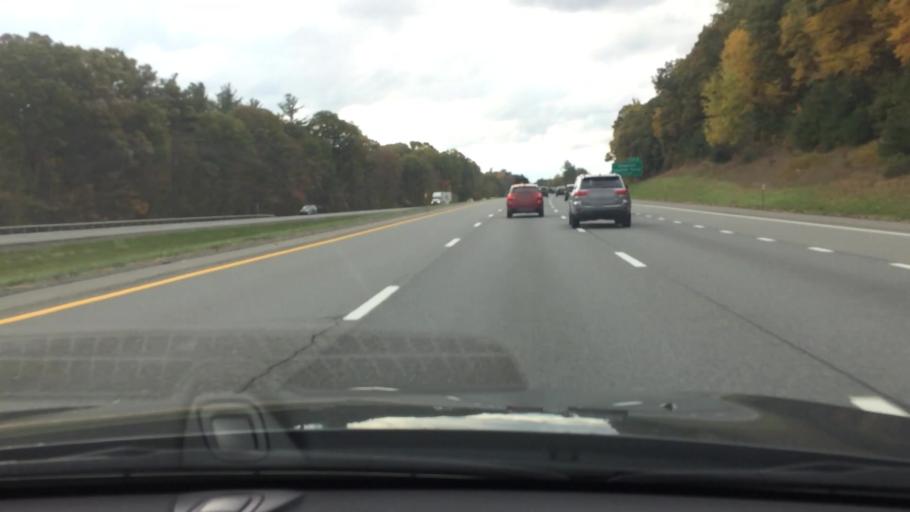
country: US
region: New York
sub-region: Saratoga County
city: Country Knolls
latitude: 42.8345
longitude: -73.7705
